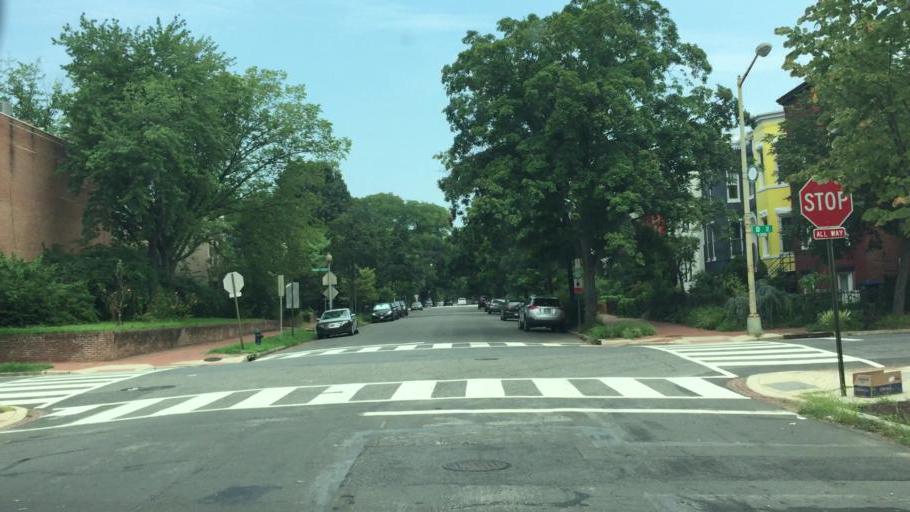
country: US
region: Washington, D.C.
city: Washington, D.C.
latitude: 38.8839
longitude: -76.9902
